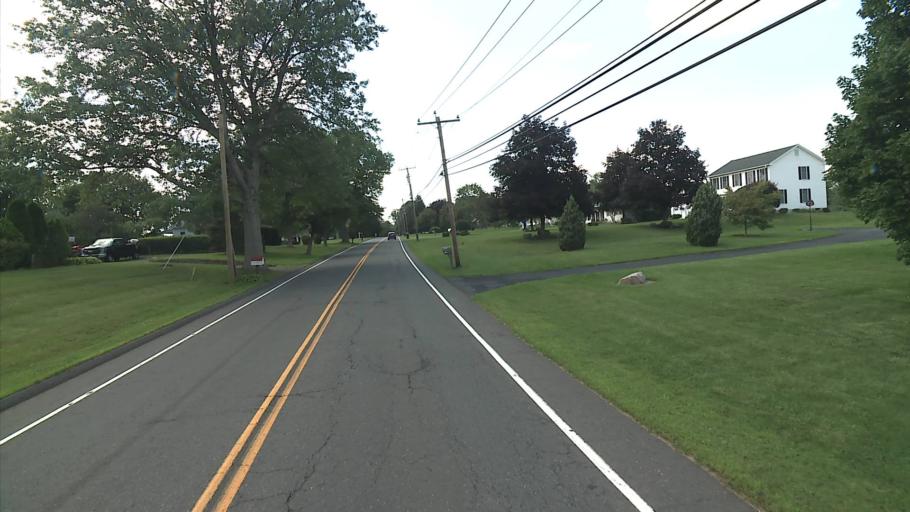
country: US
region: Connecticut
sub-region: Hartford County
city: Suffield Depot
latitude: 41.9979
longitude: -72.6303
